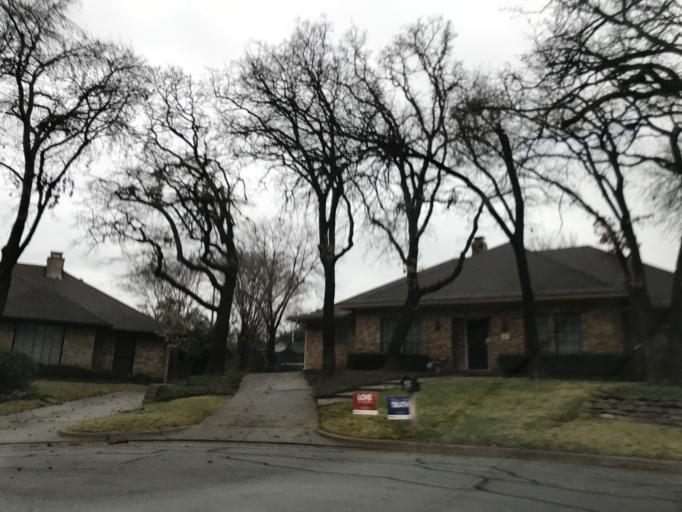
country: US
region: Texas
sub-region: Tarrant County
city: Arlington
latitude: 32.7732
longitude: -97.1062
